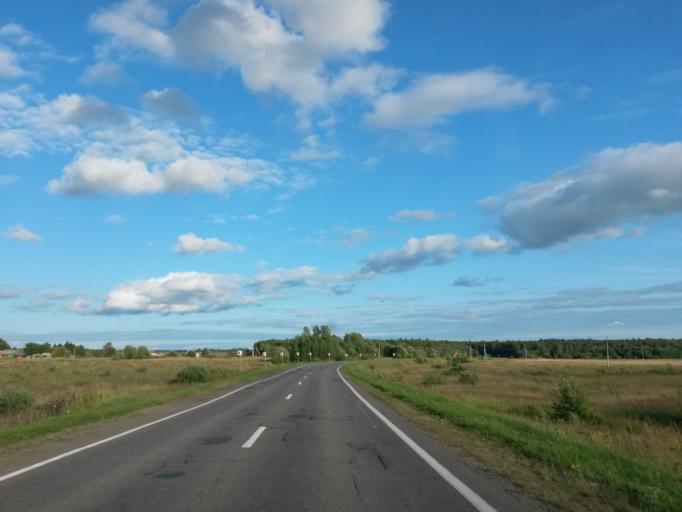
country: RU
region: Jaroslavl
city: Konstantinovskiy
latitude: 57.8648
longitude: 39.6088
